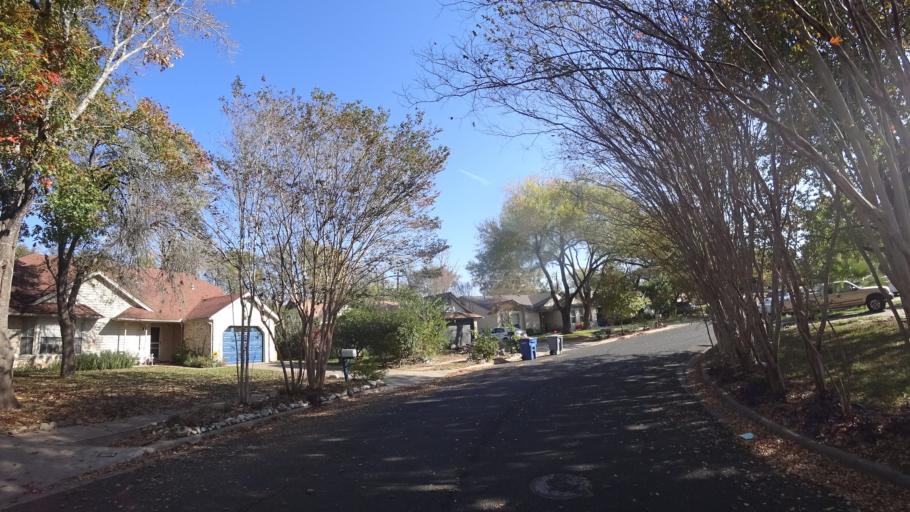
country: US
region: Texas
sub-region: Travis County
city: Barton Creek
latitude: 30.2334
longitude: -97.8535
